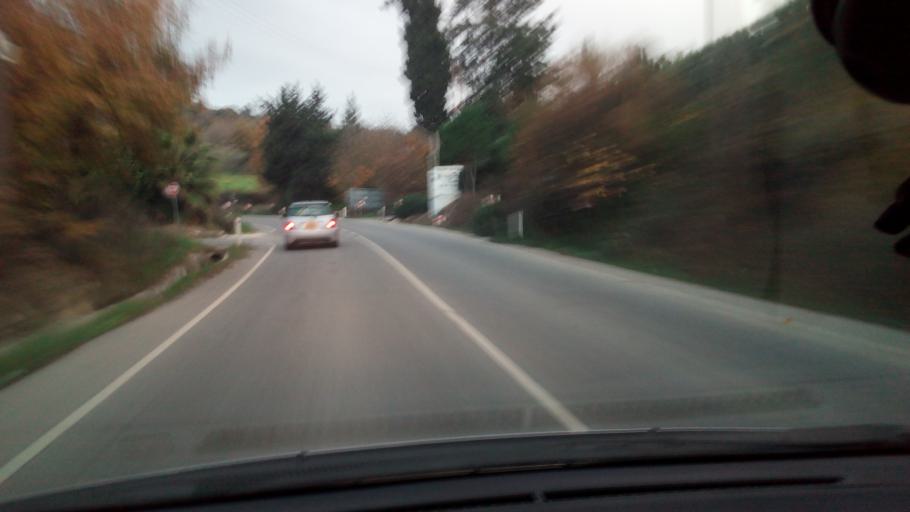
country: CY
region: Pafos
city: Pegeia
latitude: 34.9334
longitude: 32.4710
